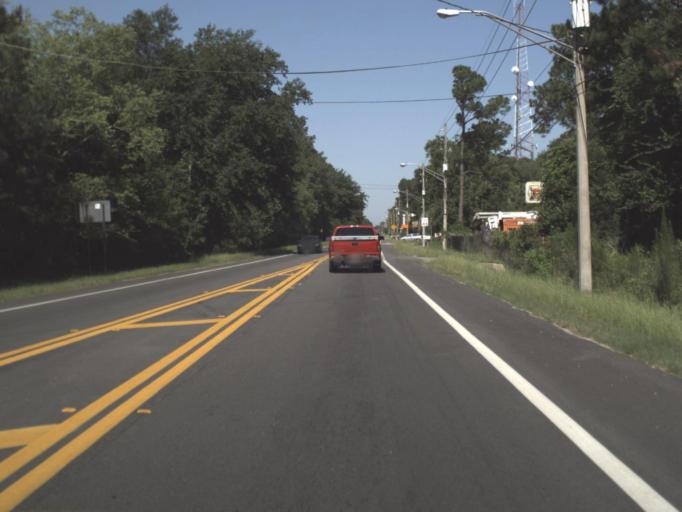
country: US
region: Florida
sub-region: Duval County
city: Jacksonville
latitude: 30.3201
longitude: -81.7945
